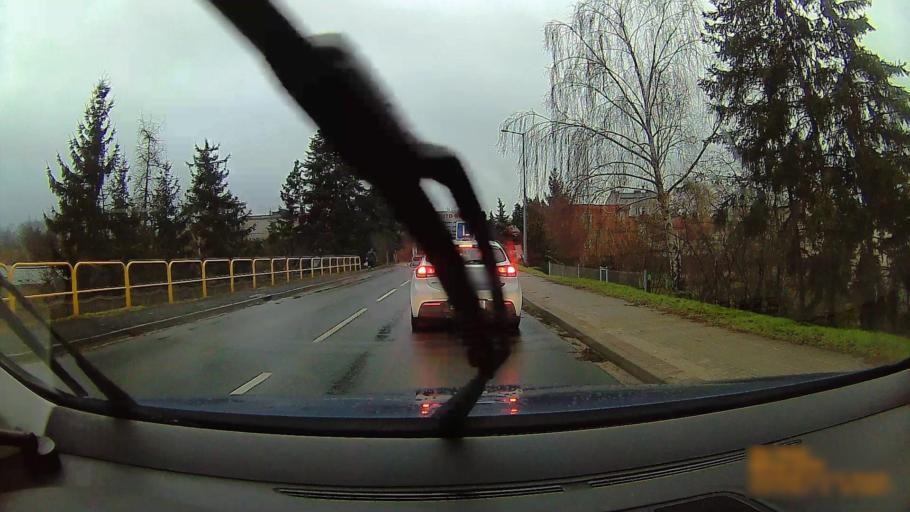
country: PL
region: Greater Poland Voivodeship
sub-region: Konin
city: Konin
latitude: 52.2051
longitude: 18.2632
